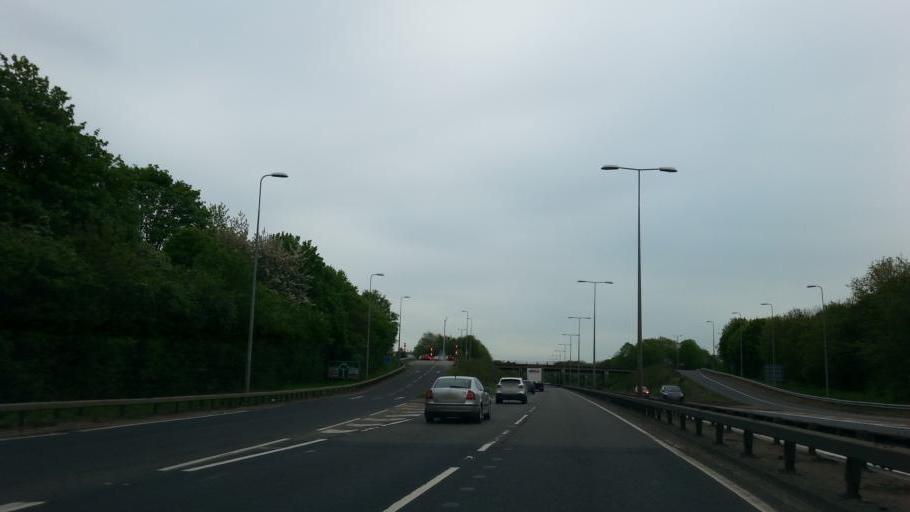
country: GB
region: England
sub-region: Peterborough
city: Marholm
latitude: 52.5906
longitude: -0.2805
